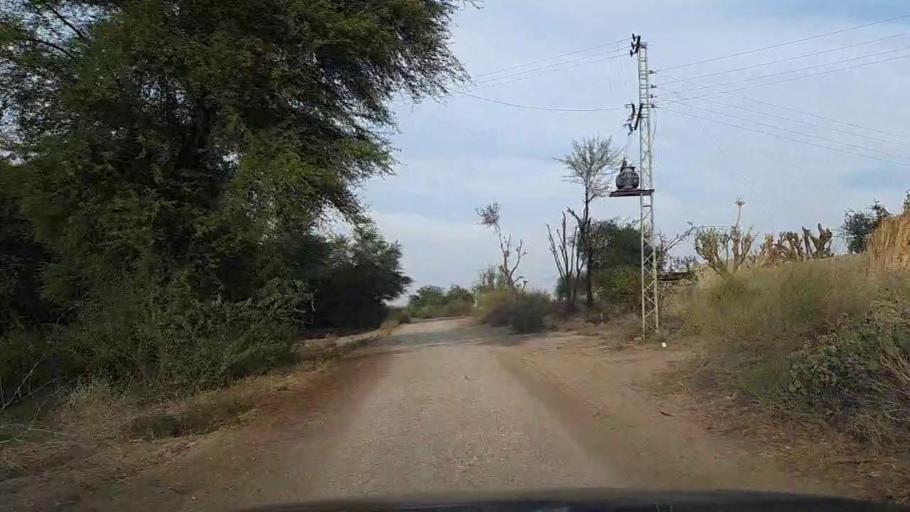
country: PK
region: Sindh
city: Jam Sahib
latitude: 26.4615
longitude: 68.5722
